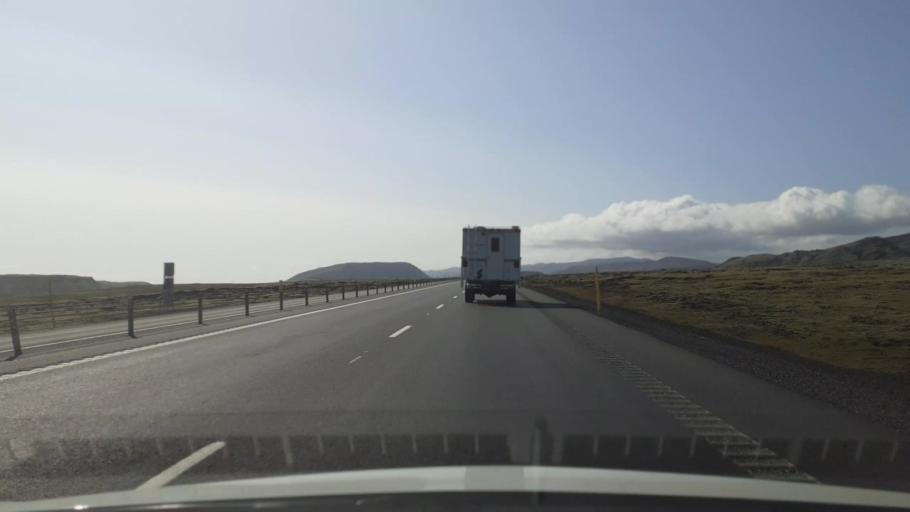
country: IS
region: South
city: Hveragerdi
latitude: 64.0203
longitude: -21.3252
